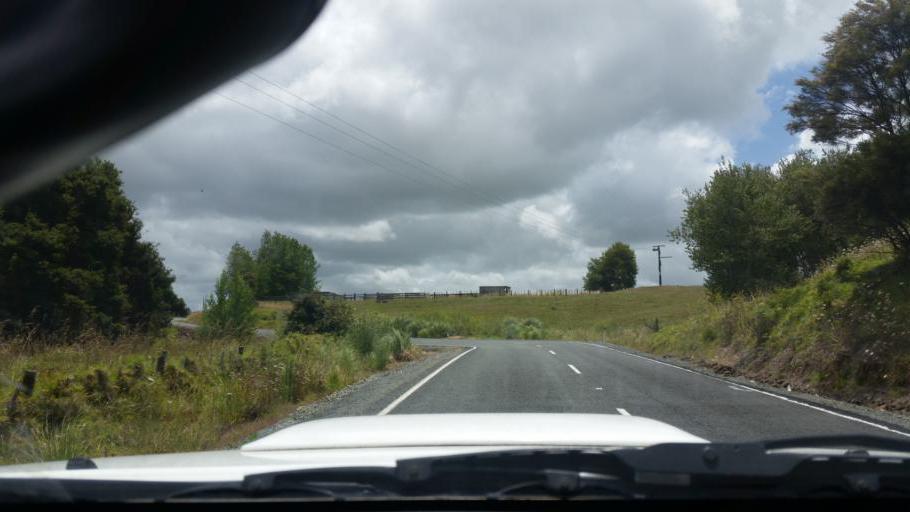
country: NZ
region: Auckland
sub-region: Auckland
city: Wellsford
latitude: -36.1273
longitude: 174.3283
